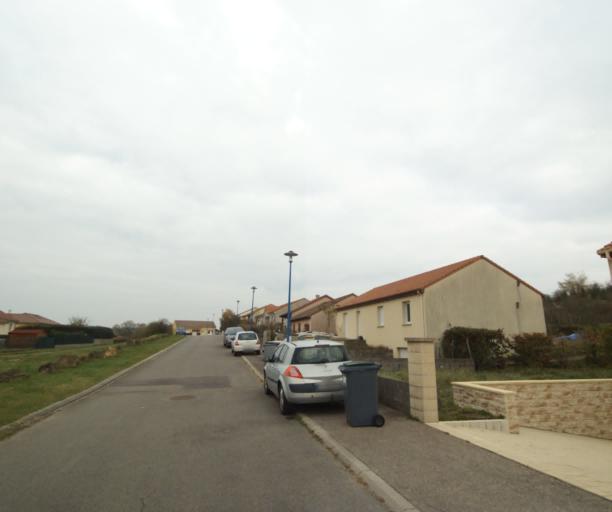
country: FR
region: Lorraine
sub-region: Departement de Meurthe-et-Moselle
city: Mancieulles
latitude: 49.2877
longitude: 5.8957
